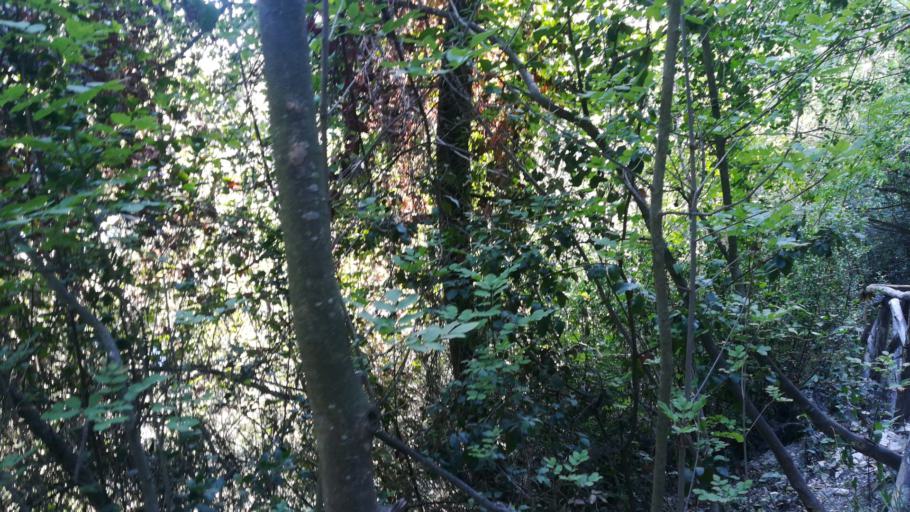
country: IT
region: The Marches
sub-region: Provincia di Ancona
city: Sirolo
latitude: 43.5229
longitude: 13.6222
